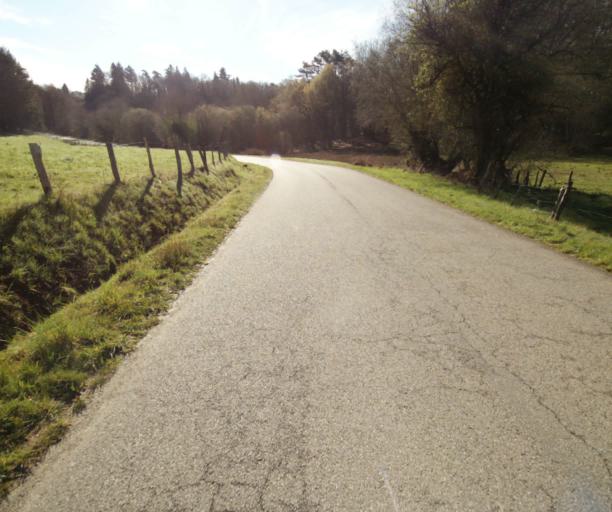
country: FR
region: Limousin
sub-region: Departement de la Correze
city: Laguenne
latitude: 45.2676
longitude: 1.8657
